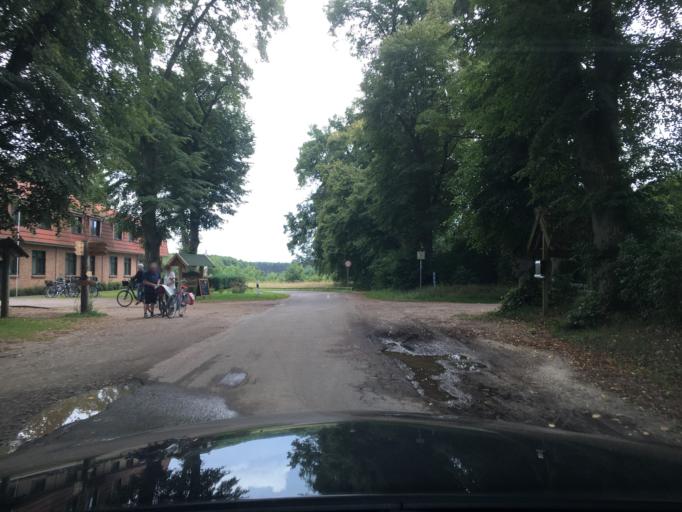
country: DE
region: Mecklenburg-Vorpommern
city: Waren
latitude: 53.4626
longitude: 12.8001
